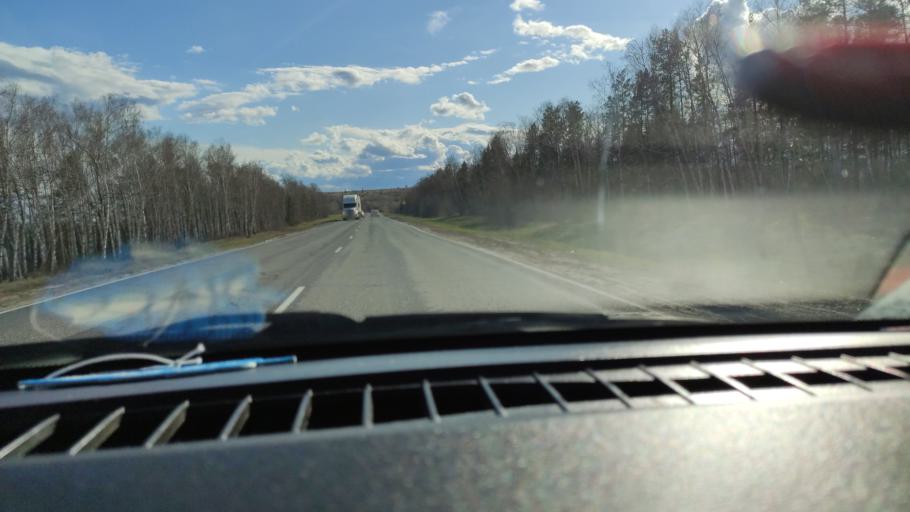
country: RU
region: Saratov
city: Sennoy
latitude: 52.1016
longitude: 46.8154
